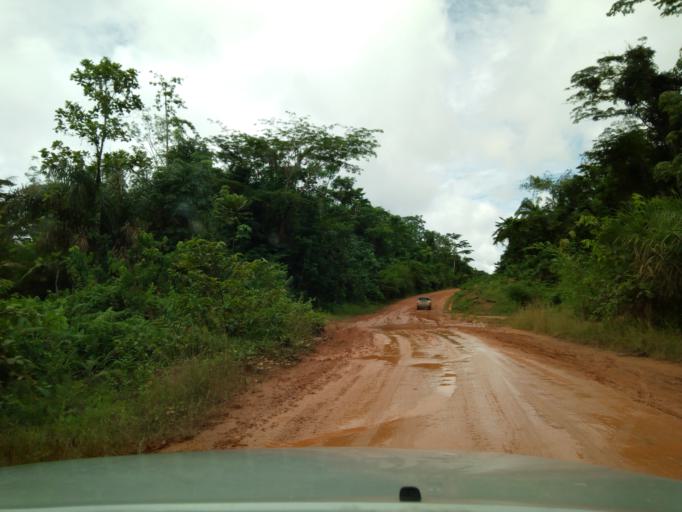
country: CI
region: Dix-Huit Montagnes
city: Toulepleu Guere
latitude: 6.7968
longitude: -8.7970
